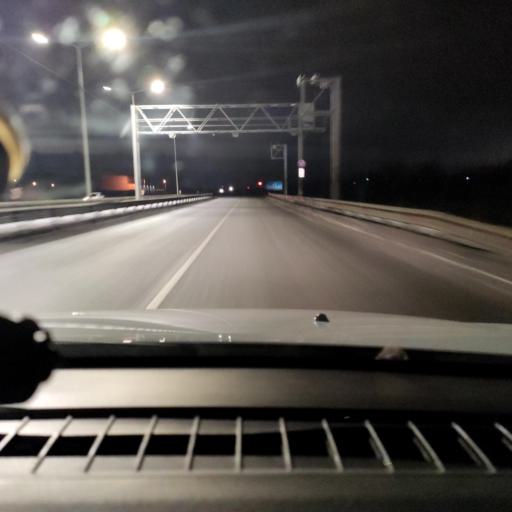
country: RU
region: Samara
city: Kinel'
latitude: 53.2616
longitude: 50.5140
